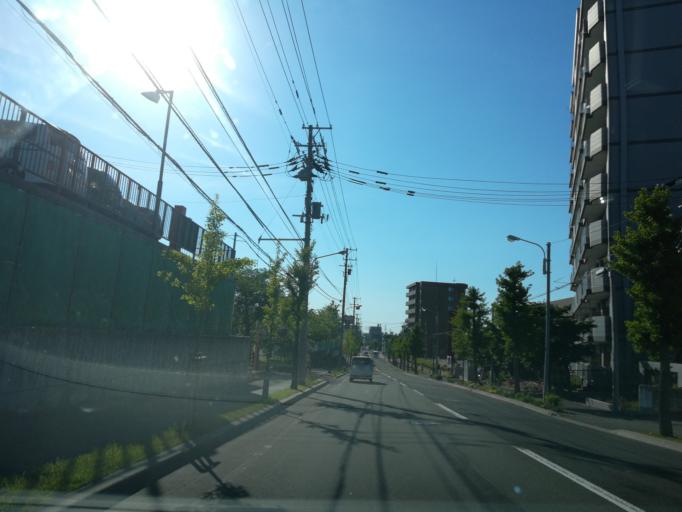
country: JP
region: Hokkaido
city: Sapporo
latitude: 43.0212
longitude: 141.4463
